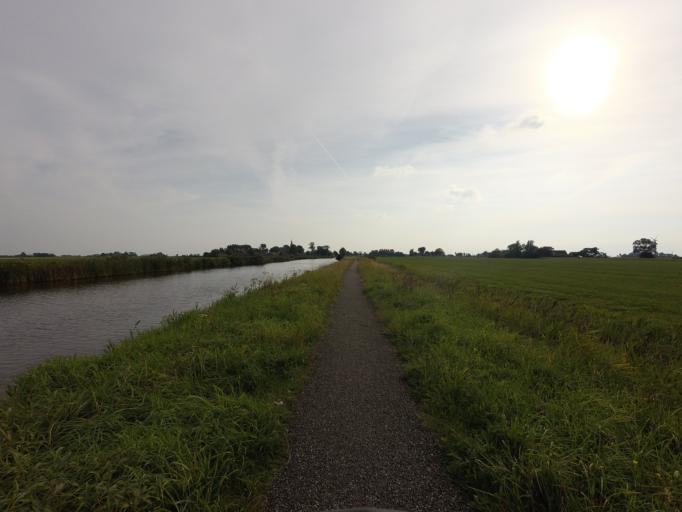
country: NL
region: Friesland
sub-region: Sudwest Fryslan
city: Bolsward
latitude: 53.0472
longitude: 5.5041
